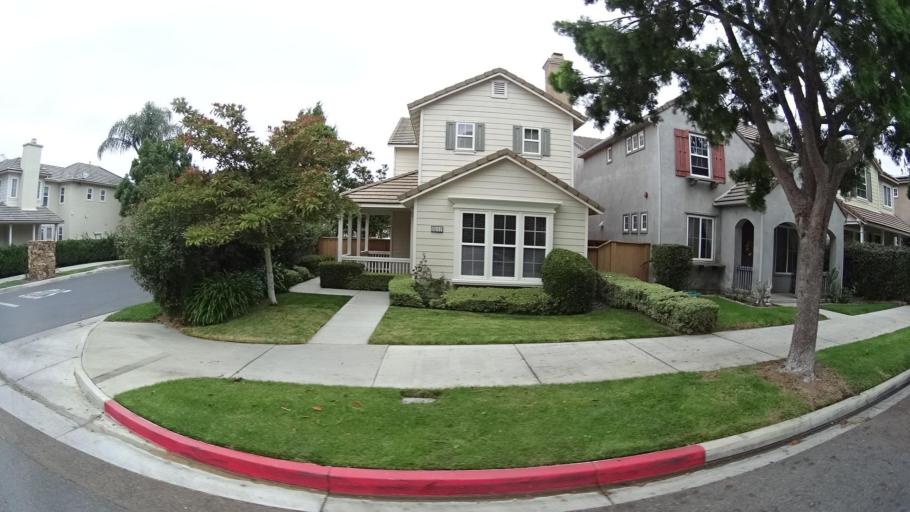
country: US
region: California
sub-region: San Diego County
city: Fairbanks Ranch
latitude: 33.0150
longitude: -117.1181
